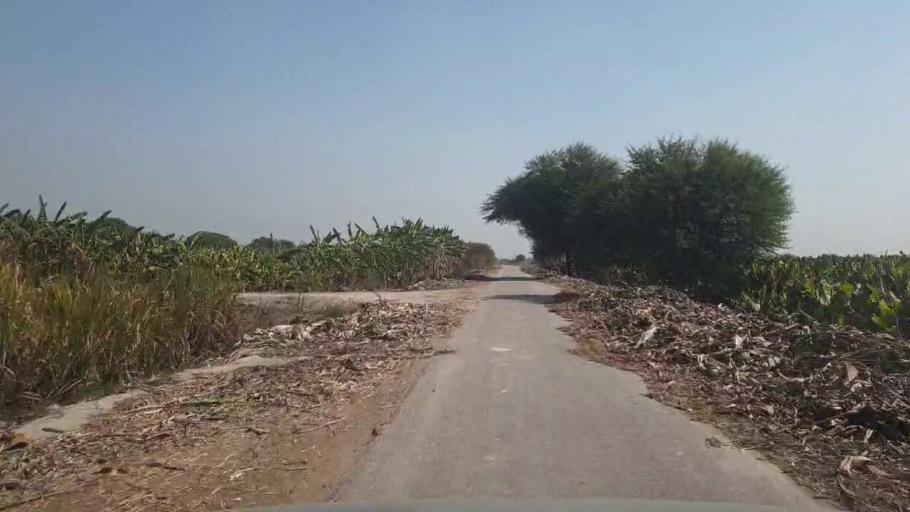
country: PK
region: Sindh
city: Chambar
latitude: 25.2418
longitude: 68.8569
